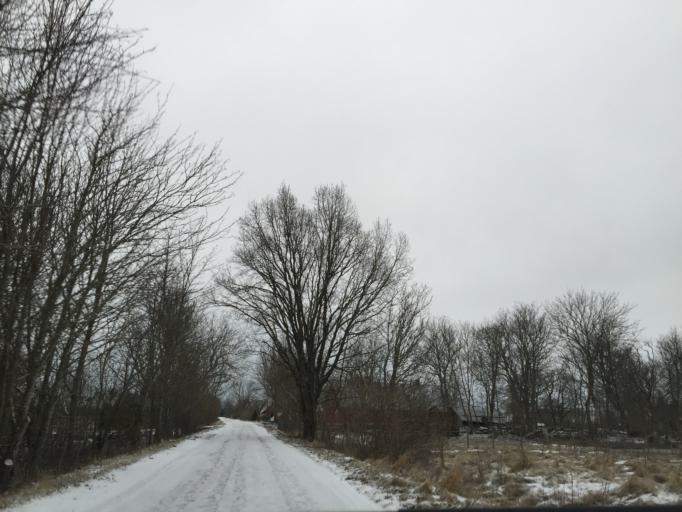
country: EE
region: Saare
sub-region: Orissaare vald
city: Orissaare
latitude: 58.5499
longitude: 23.3903
